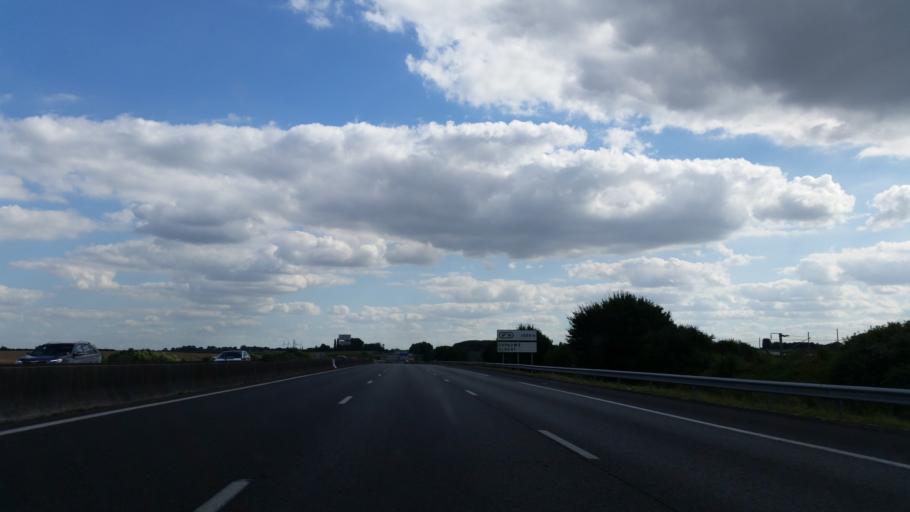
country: FR
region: Nord-Pas-de-Calais
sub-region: Departement du Pas-de-Calais
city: Bapaume
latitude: 50.1144
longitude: 2.8715
